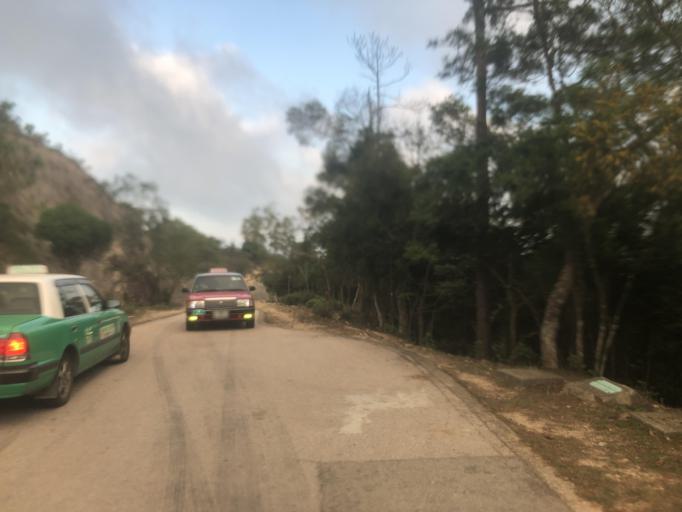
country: HK
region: Sai Kung
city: Sai Kung
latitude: 22.3626
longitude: 114.3497
